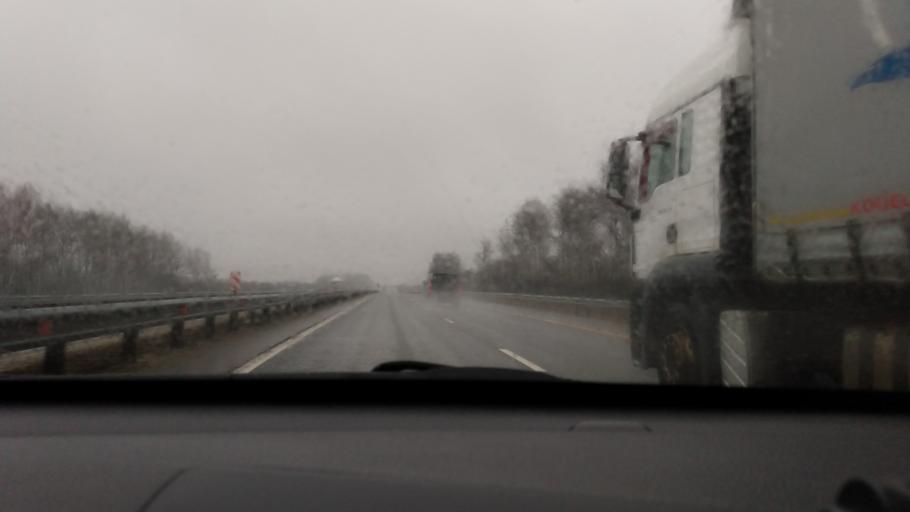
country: RU
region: Tula
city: Gritsovskiy
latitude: 54.2638
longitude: 38.1553
